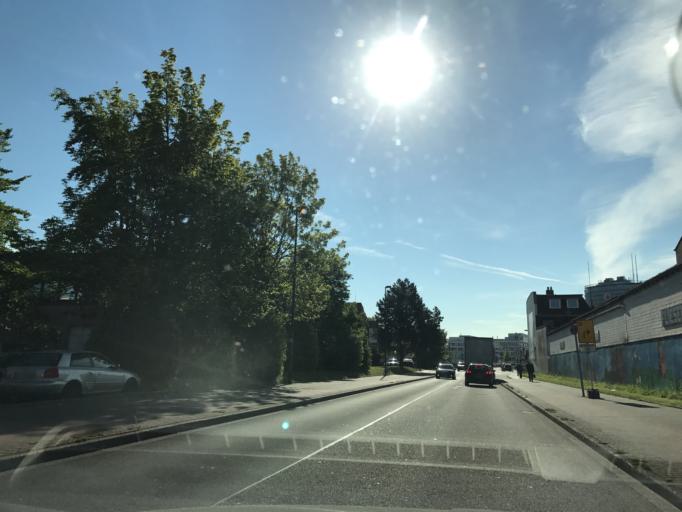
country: DE
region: North Rhine-Westphalia
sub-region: Regierungsbezirk Dusseldorf
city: Dusseldorf
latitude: 51.2379
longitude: 6.7254
